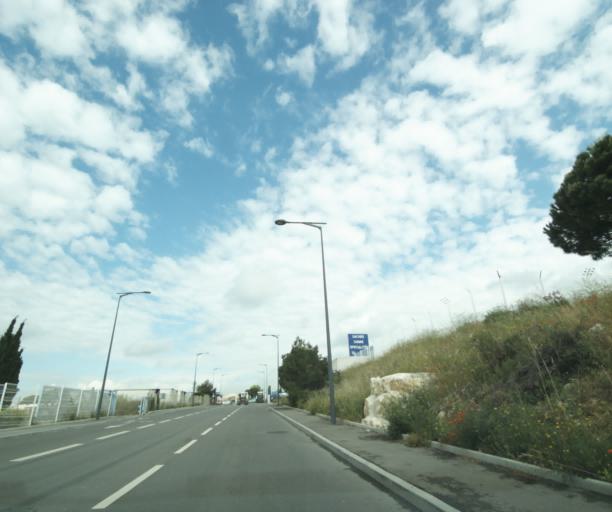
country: FR
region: Provence-Alpes-Cote d'Azur
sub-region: Departement des Bouches-du-Rhone
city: Vitrolles
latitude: 43.4401
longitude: 5.2420
